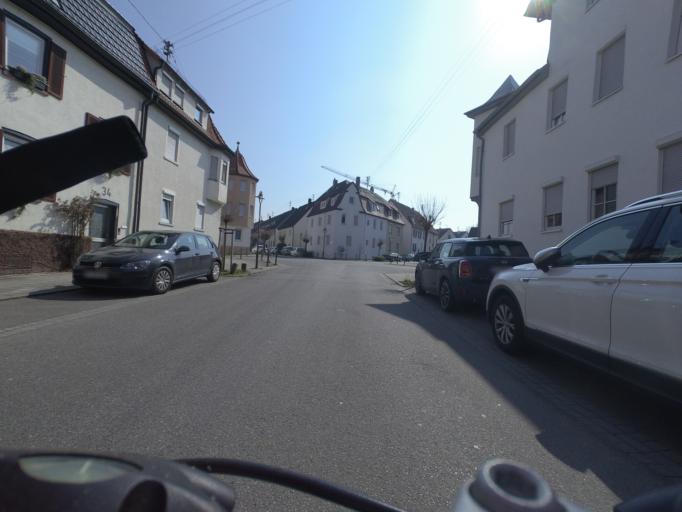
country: DE
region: Baden-Wuerttemberg
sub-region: Regierungsbezirk Stuttgart
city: Nurtingen
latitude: 48.6241
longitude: 9.3342
